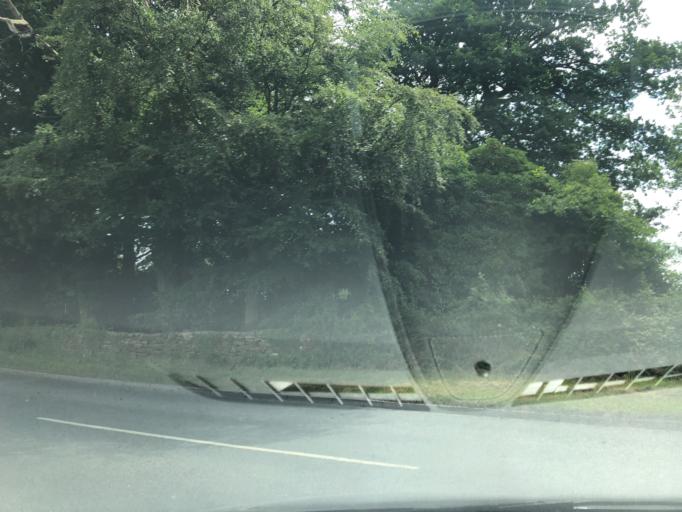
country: GB
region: England
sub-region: North Yorkshire
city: Strensall
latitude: 54.1430
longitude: -1.0010
